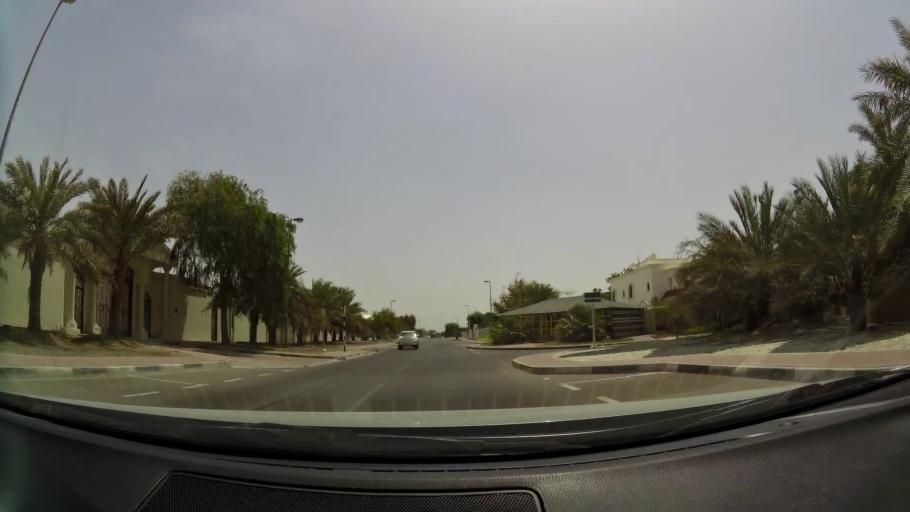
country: AE
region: Abu Dhabi
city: Al Ain
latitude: 24.1810
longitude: 55.7228
